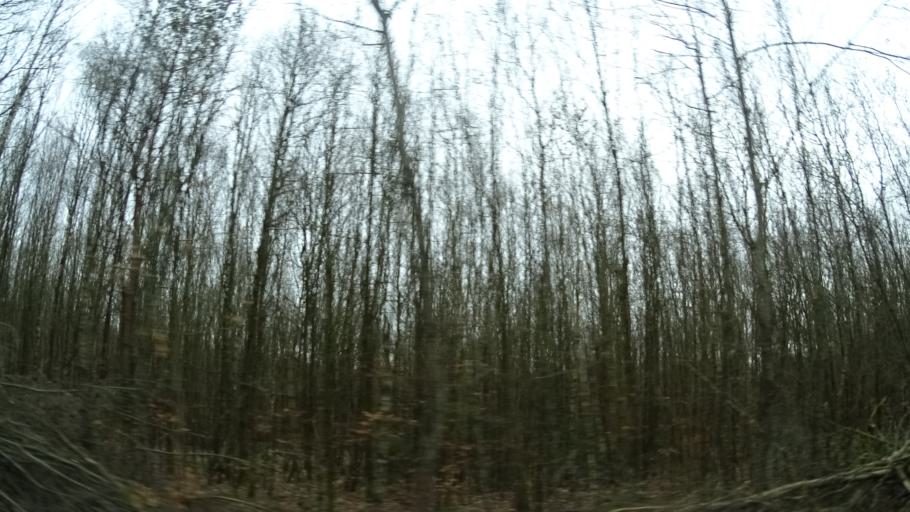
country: DE
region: Rheinland-Pfalz
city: Ippenschied
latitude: 49.8794
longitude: 7.6184
